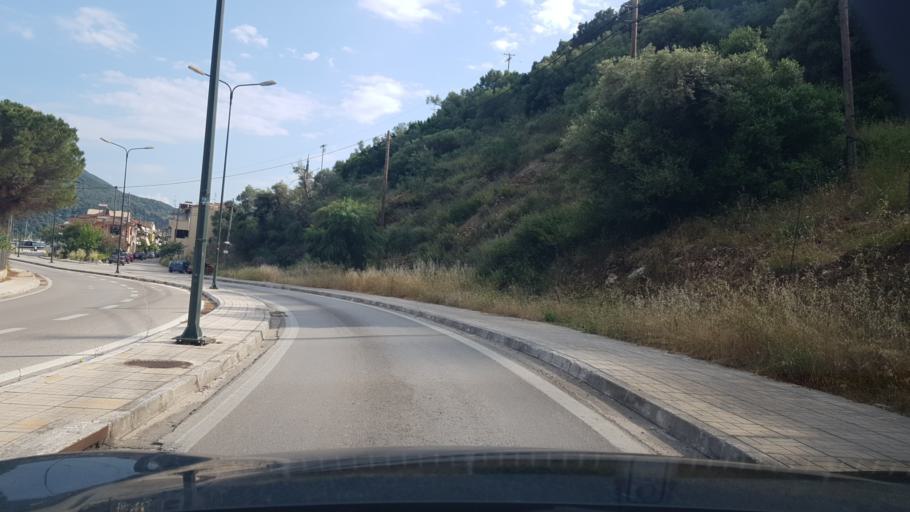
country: GR
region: Ionian Islands
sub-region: Lefkada
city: Nidri
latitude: 38.6910
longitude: 20.6983
